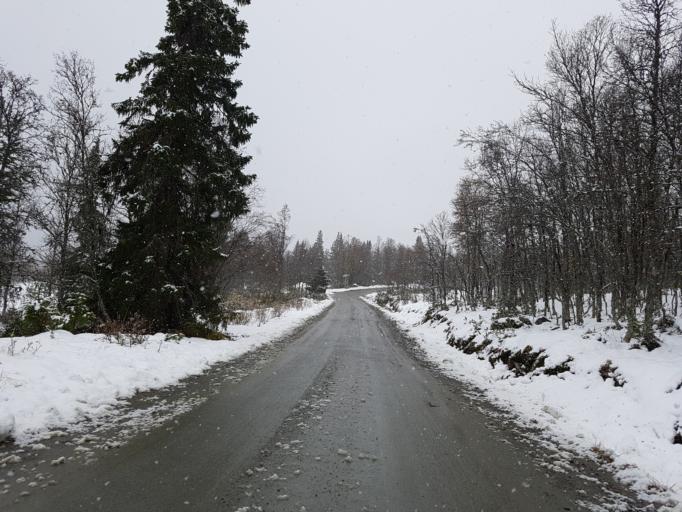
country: NO
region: Oppland
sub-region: Sel
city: Otta
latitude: 61.7907
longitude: 9.7190
